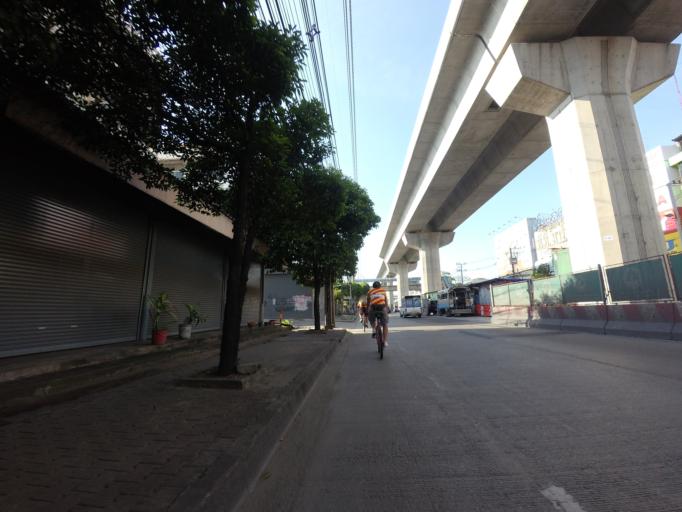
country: TH
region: Samut Prakan
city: Samut Prakan
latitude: 13.6405
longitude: 100.5935
